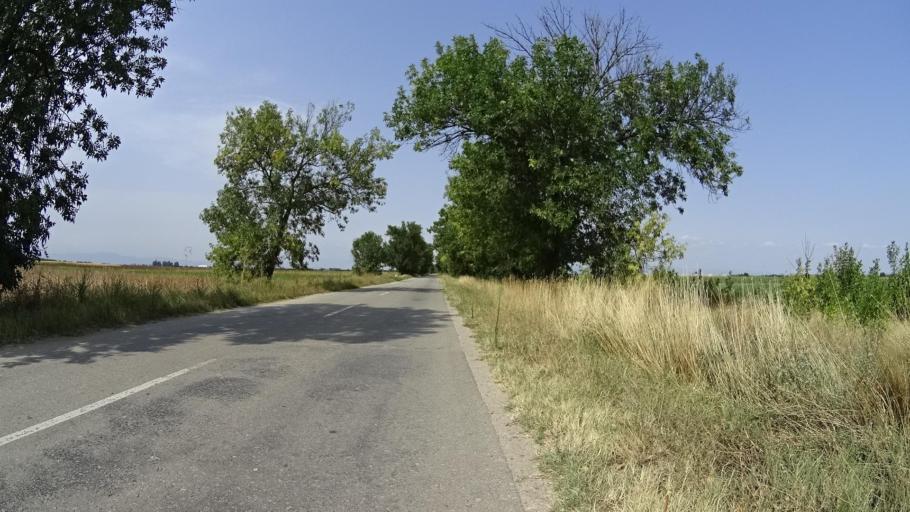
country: BG
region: Plovdiv
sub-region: Obshtina Plovdiv
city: Plovdiv
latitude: 42.2500
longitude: 24.7972
